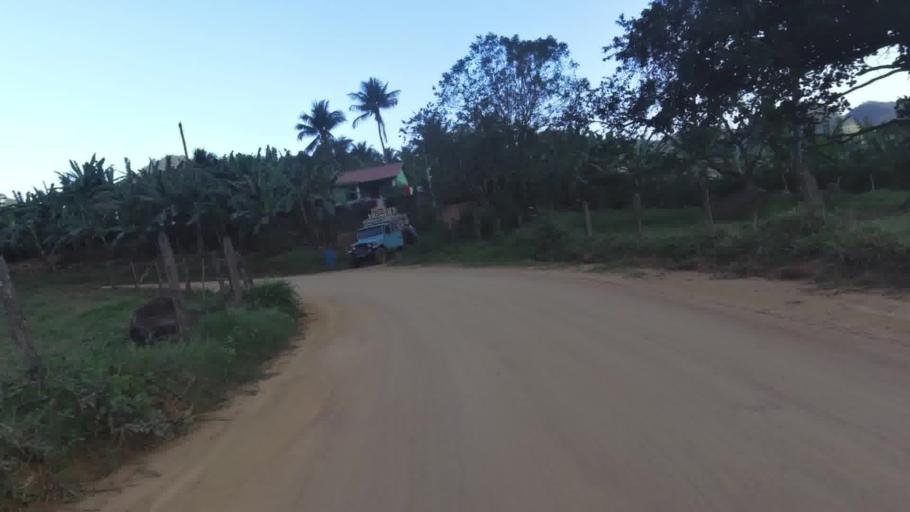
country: BR
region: Espirito Santo
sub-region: Alfredo Chaves
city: Alfredo Chaves
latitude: -20.5896
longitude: -40.7014
